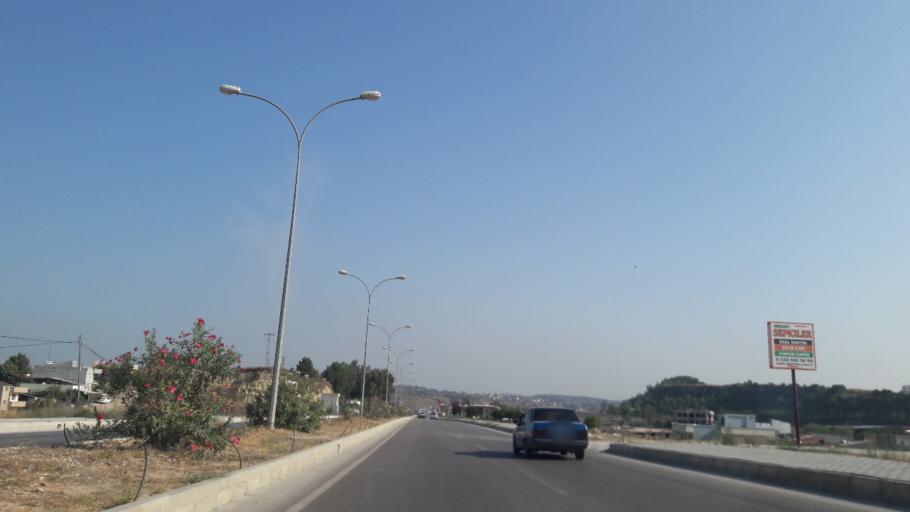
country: TR
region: Adana
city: Yuregir
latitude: 37.0525
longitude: 35.4403
